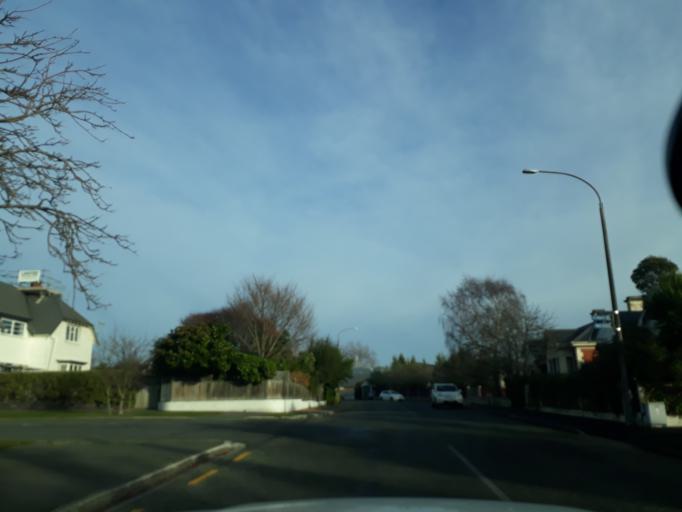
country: NZ
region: Canterbury
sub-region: Timaru District
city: Timaru
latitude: -44.3879
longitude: 171.2405
